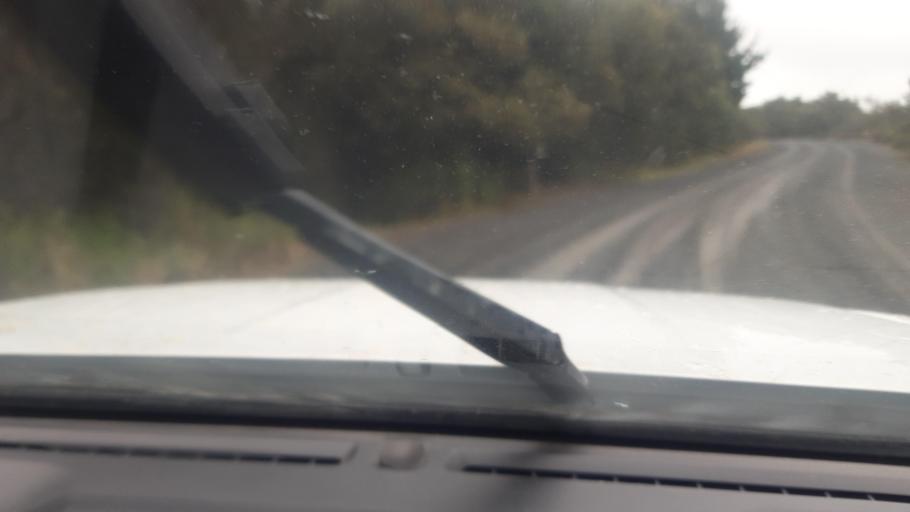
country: NZ
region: Northland
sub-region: Far North District
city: Kaitaia
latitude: -34.9863
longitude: 173.2125
